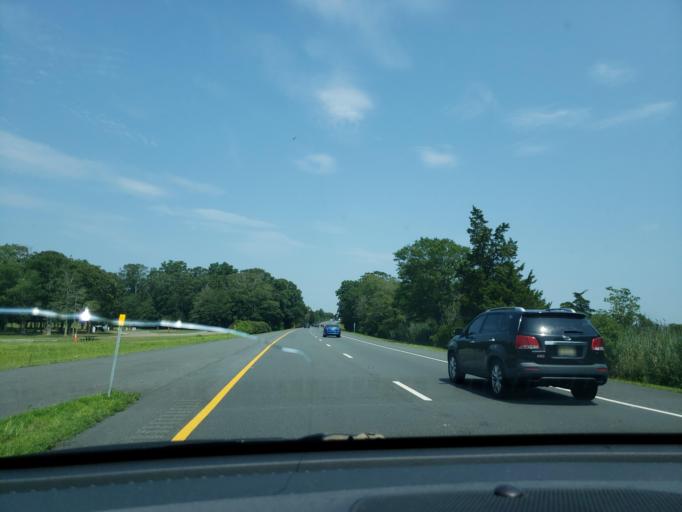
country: US
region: New Jersey
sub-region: Cape May County
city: Sea Isle City
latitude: 39.2320
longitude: -74.6716
